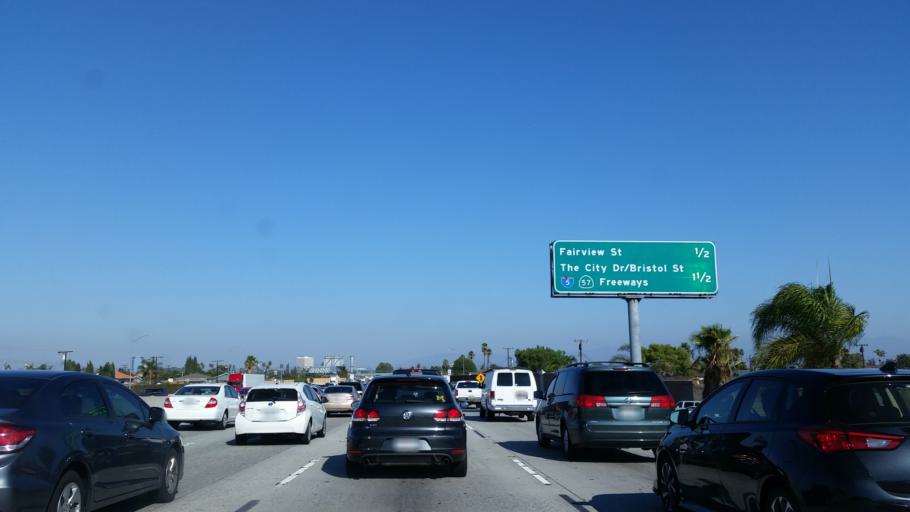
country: US
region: California
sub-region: Orange County
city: Garden Grove
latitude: 33.7681
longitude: -117.9188
